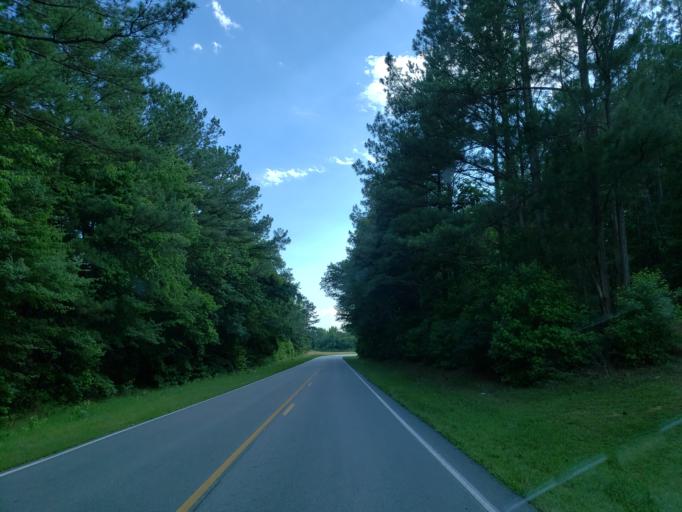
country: US
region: Georgia
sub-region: Polk County
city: Rockmart
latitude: 33.8980
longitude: -85.0821
